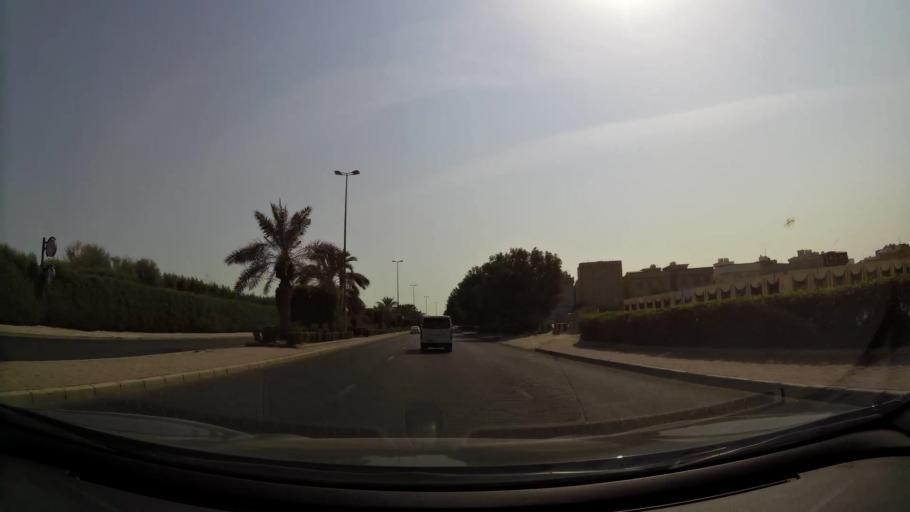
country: KW
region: Al Ahmadi
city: Al Manqaf
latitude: 29.1140
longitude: 48.1353
